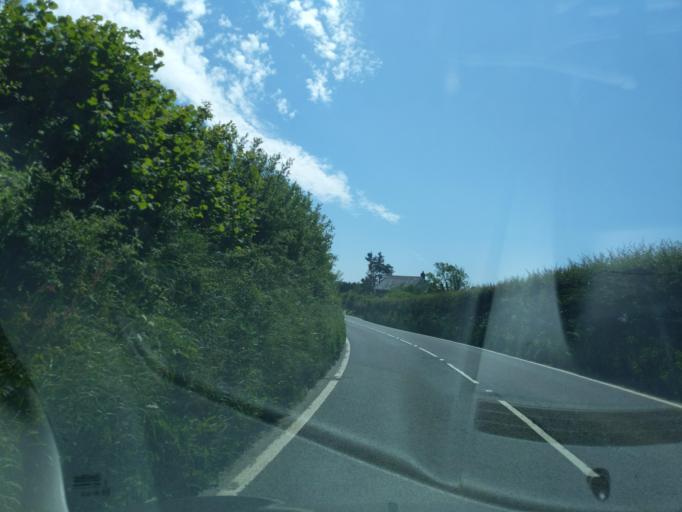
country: GB
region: England
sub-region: Cornwall
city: Camelford
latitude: 50.6106
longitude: -4.6887
